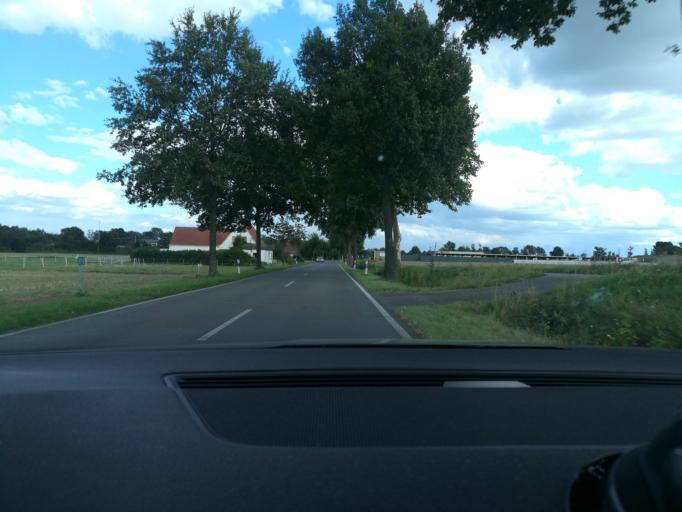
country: DE
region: North Rhine-Westphalia
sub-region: Regierungsbezirk Detmold
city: Hille
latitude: 52.3092
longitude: 8.7320
